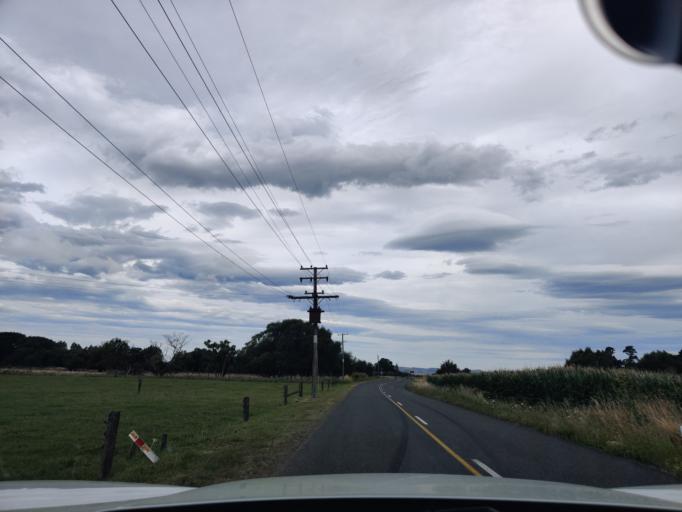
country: NZ
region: Wellington
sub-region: Masterton District
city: Masterton
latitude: -41.0347
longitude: 175.4925
